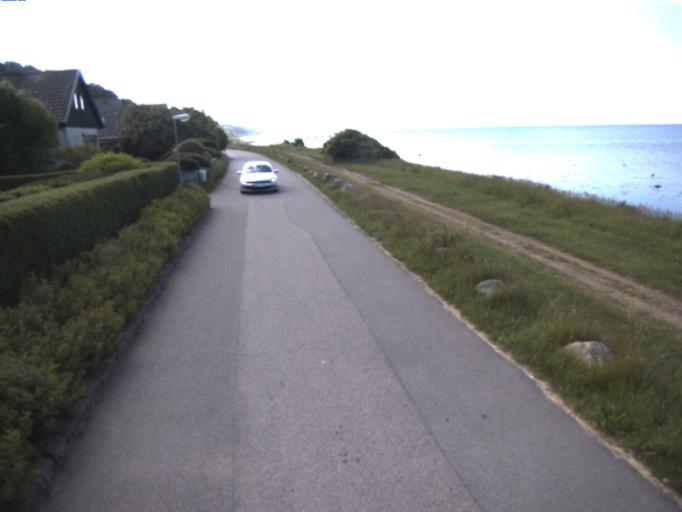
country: DK
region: Capital Region
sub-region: Helsingor Kommune
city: Helsingor
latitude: 56.0930
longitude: 12.6418
